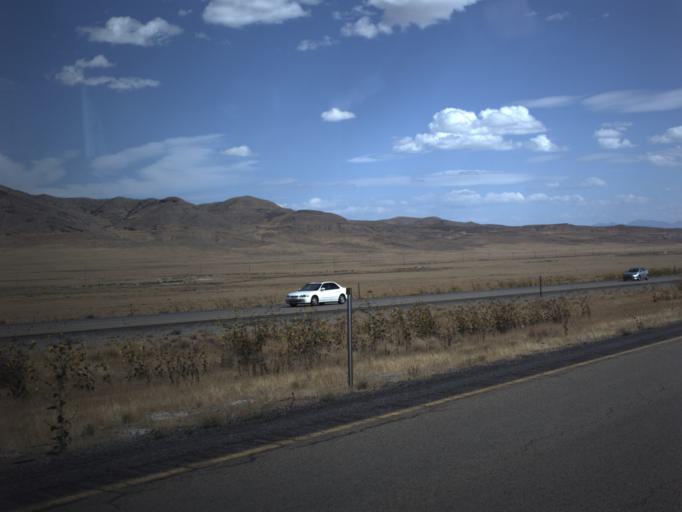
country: US
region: Utah
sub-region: Tooele County
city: Grantsville
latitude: 40.8167
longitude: -112.8803
